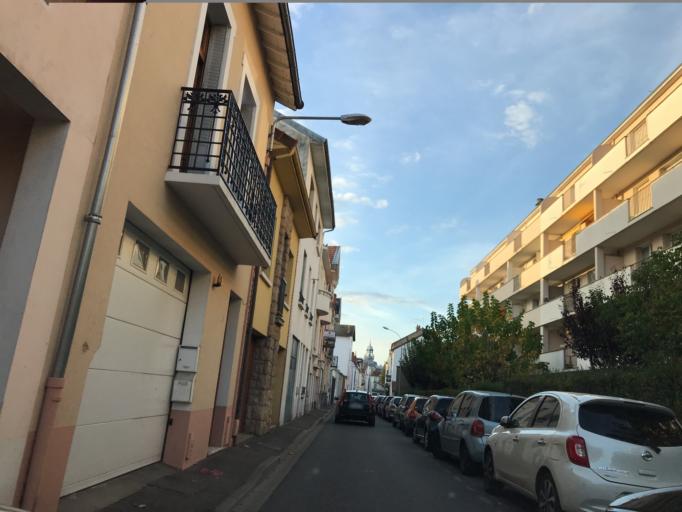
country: FR
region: Auvergne
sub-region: Departement de l'Allier
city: Vichy
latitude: 46.1208
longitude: 3.4308
